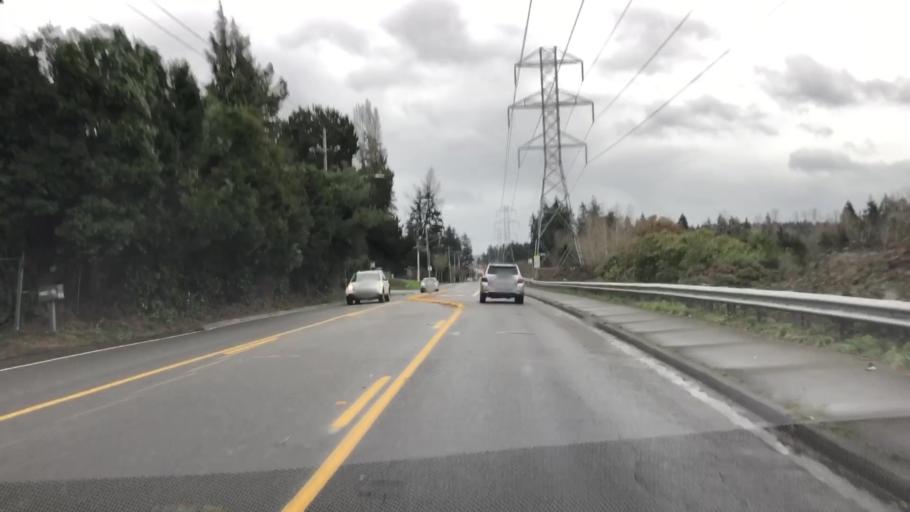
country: US
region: Washington
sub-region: King County
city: Kingsgate
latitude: 47.7425
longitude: -122.1751
